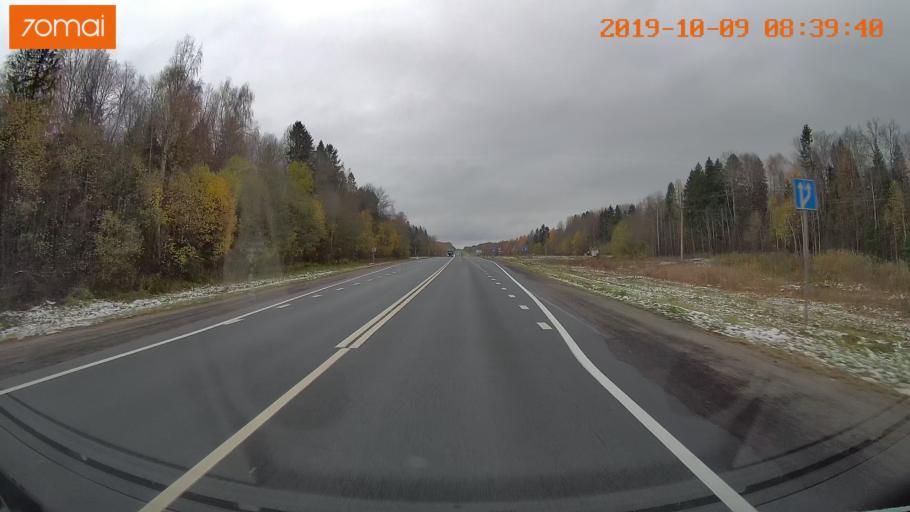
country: RU
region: Vologda
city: Gryazovets
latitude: 58.9751
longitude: 40.1501
